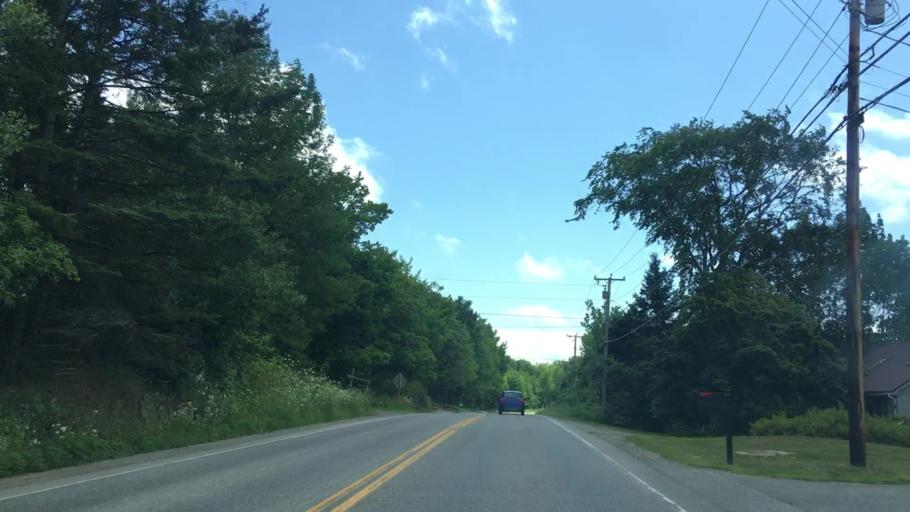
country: US
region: Maine
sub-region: Penobscot County
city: Hermon
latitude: 44.8036
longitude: -68.8975
